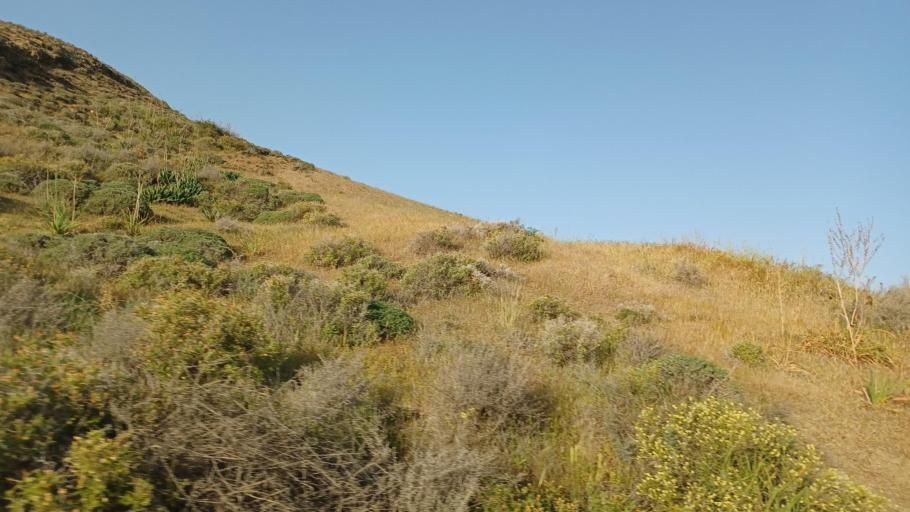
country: CY
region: Lefkosia
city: Astromeritis
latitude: 35.0758
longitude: 33.0241
